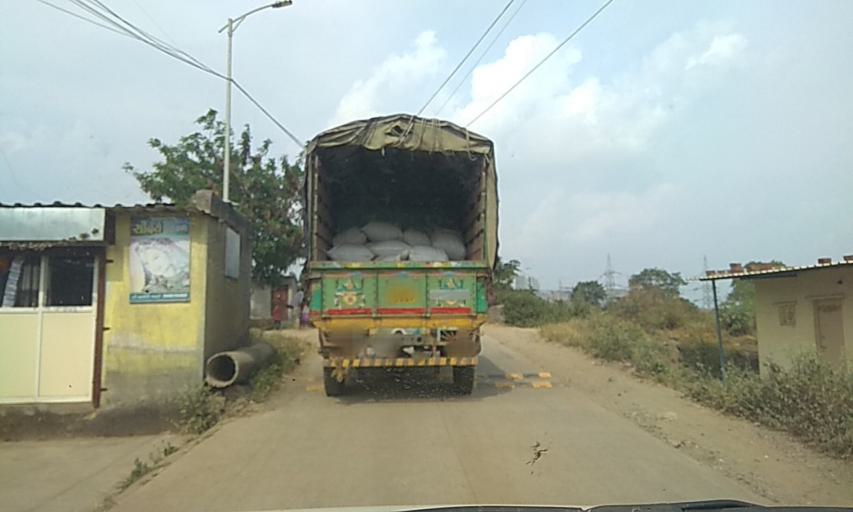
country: IN
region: Maharashtra
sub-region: Pune Division
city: Pimpri
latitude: 18.5848
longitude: 73.7059
